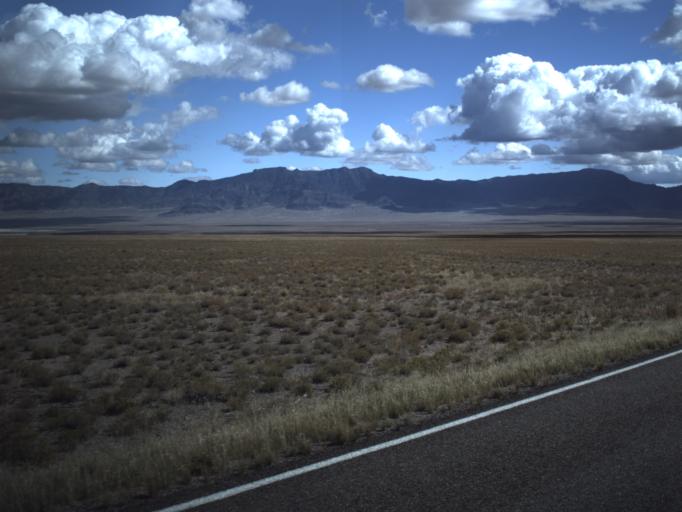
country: US
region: Utah
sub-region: Beaver County
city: Milford
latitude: 38.5763
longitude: -113.8008
